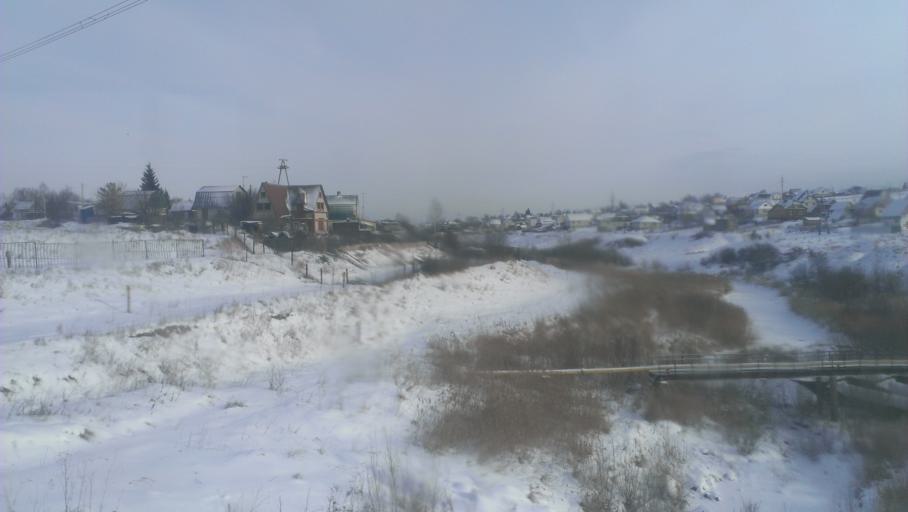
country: RU
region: Altai Krai
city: Gon'ba
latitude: 53.4156
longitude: 83.5503
